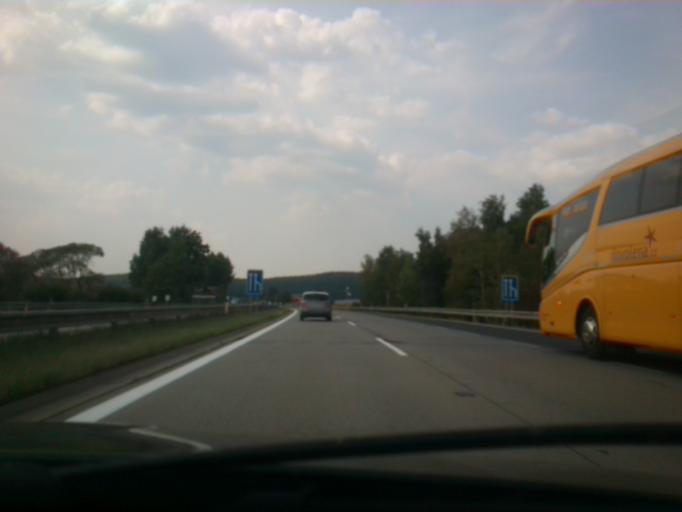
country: CZ
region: Central Bohemia
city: Divisov
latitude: 49.8274
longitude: 14.8658
